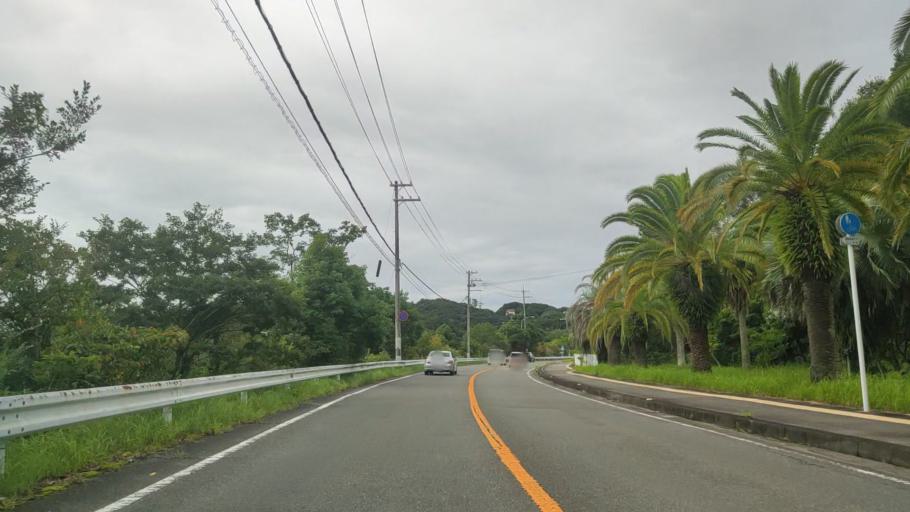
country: JP
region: Wakayama
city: Tanabe
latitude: 33.6913
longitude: 135.3846
